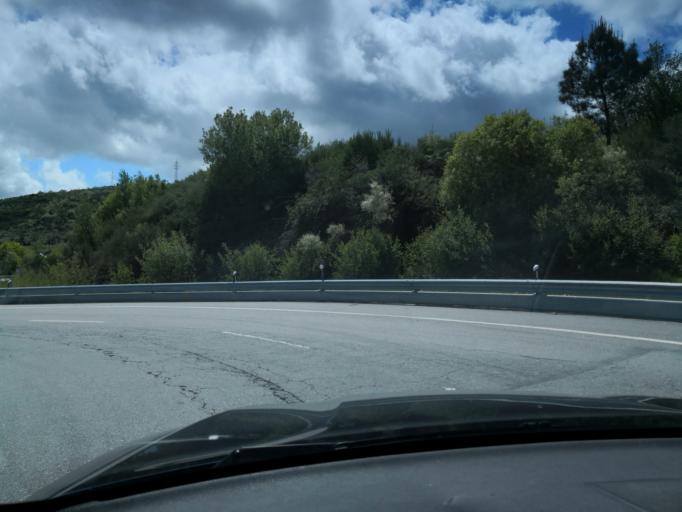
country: PT
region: Vila Real
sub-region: Vila Real
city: Vila Real
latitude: 41.3776
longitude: -7.7172
